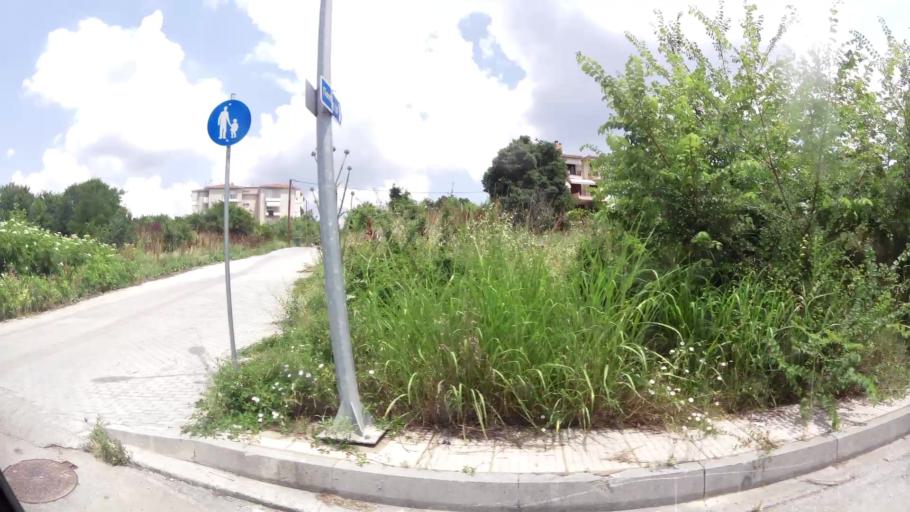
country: GR
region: West Macedonia
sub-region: Nomos Kozanis
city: Kozani
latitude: 40.2923
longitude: 21.7926
